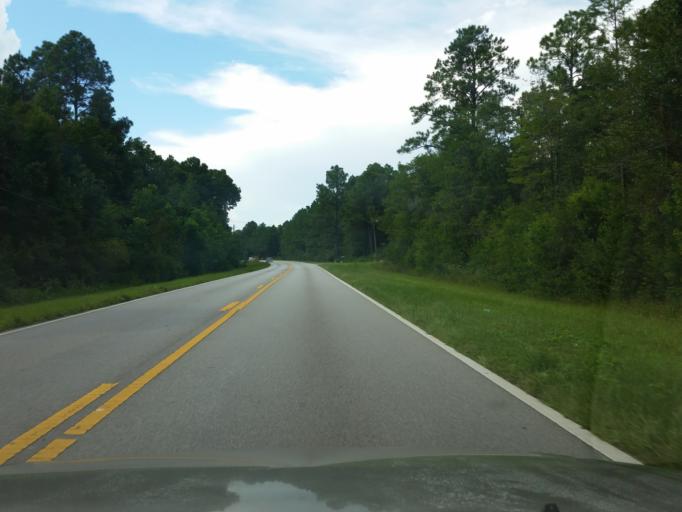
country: US
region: Florida
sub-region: Escambia County
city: Myrtle Grove
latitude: 30.3940
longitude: -87.4015
